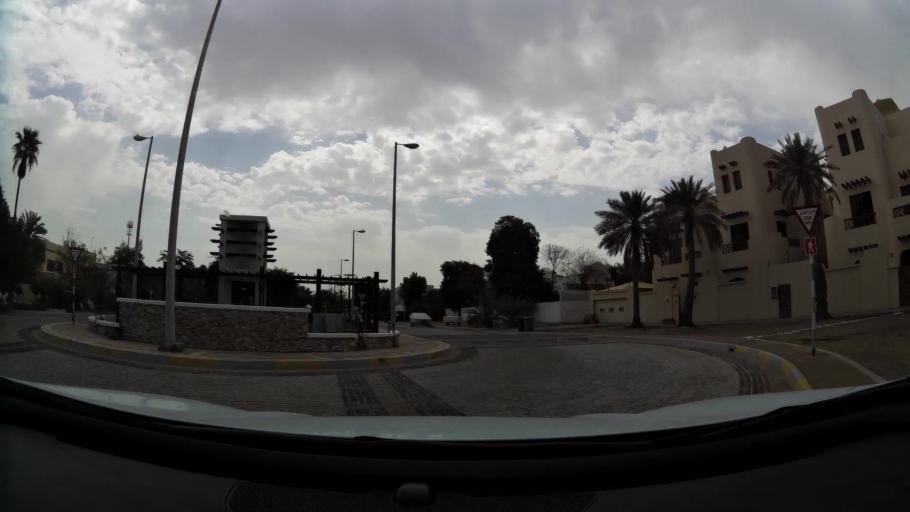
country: AE
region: Abu Dhabi
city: Abu Dhabi
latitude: 24.4507
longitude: 54.3582
